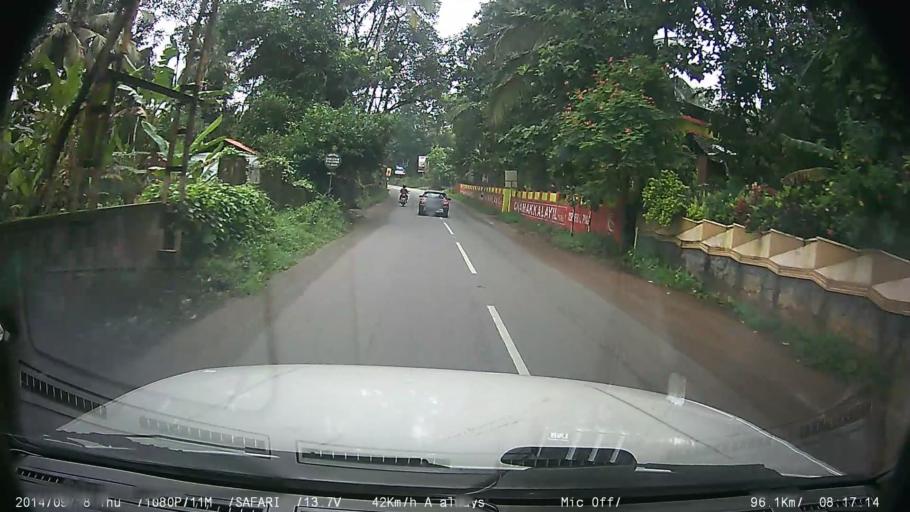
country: IN
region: Kerala
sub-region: Kottayam
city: Kottayam
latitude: 9.6404
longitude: 76.6068
